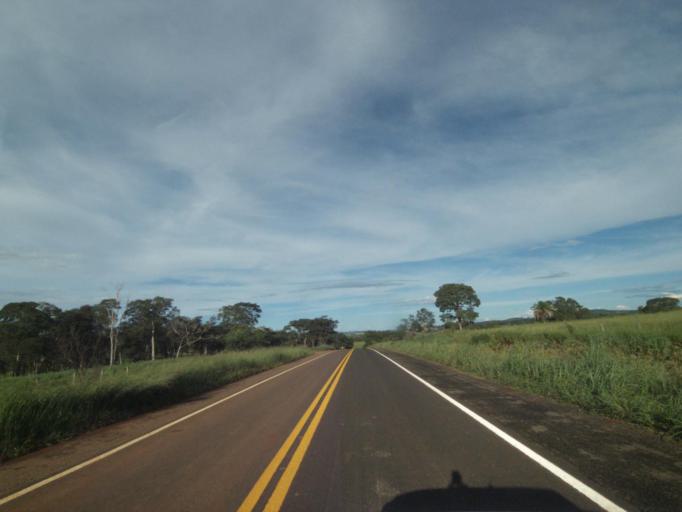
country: BR
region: Goias
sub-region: Itaberai
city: Itaberai
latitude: -15.9090
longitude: -49.5748
